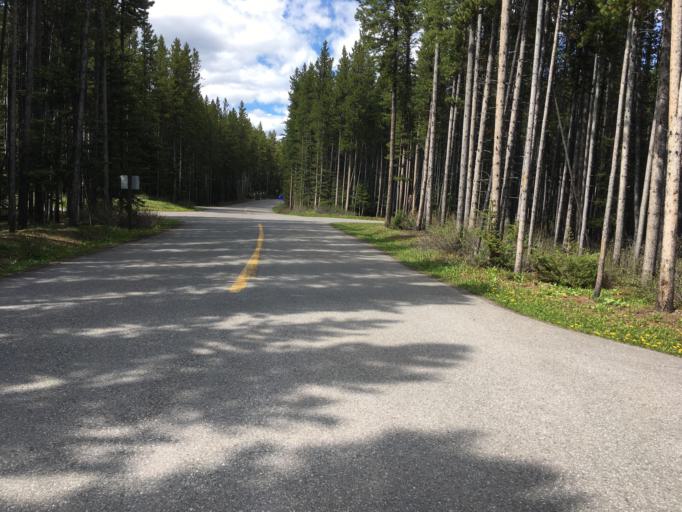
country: CA
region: Alberta
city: Canmore
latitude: 50.6284
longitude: -115.0996
